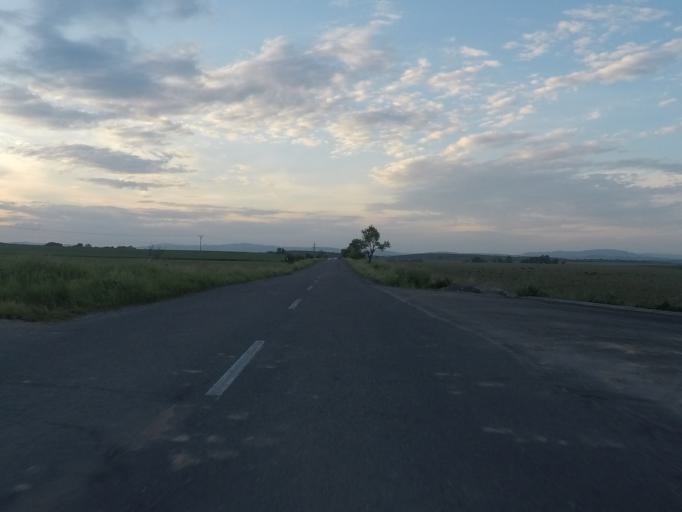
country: SK
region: Banskobystricky
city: Poltar
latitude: 48.3542
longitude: 19.8326
